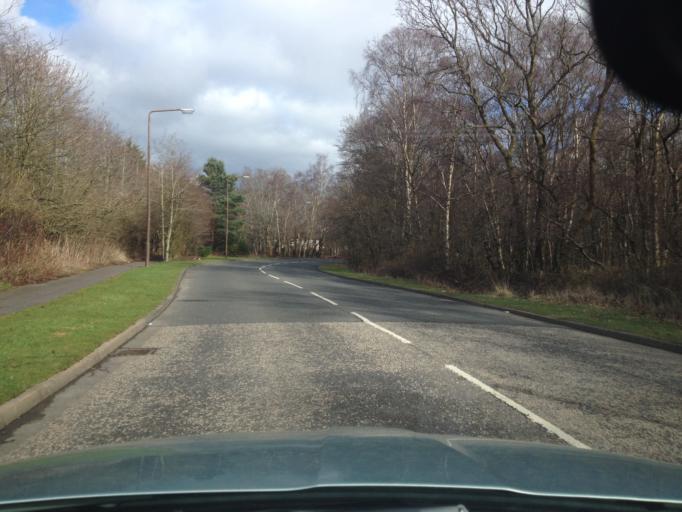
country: GB
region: Scotland
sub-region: West Lothian
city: Livingston
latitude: 55.8645
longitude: -3.5245
